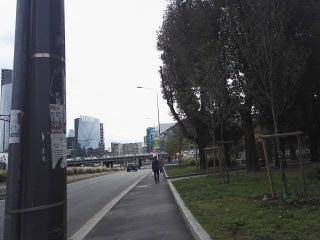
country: IT
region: Lombardy
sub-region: Citta metropolitana di Milano
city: Milano
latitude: 45.4850
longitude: 9.1842
